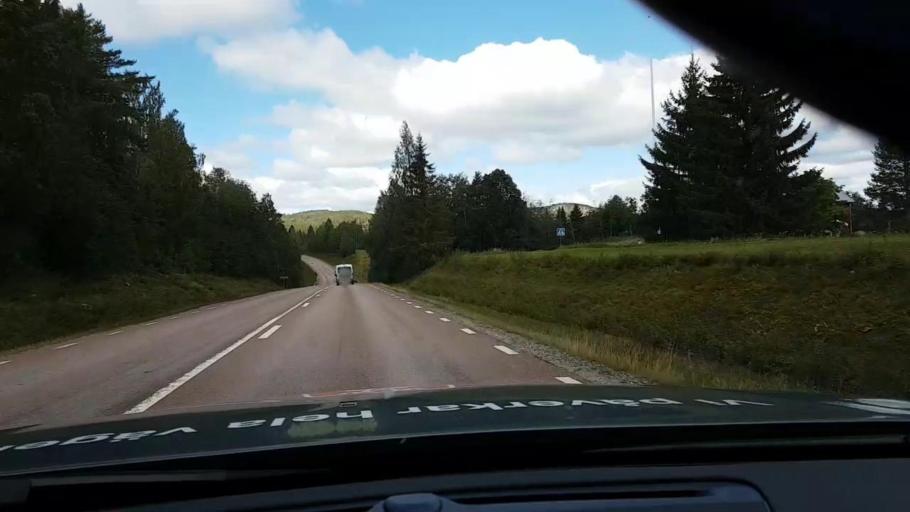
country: SE
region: Vaesternorrland
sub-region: OErnskoeldsviks Kommun
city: Bjasta
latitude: 63.3712
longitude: 18.4379
